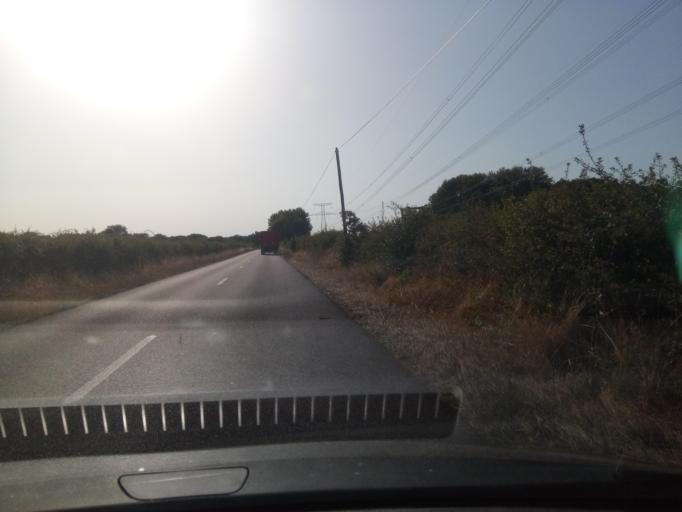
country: FR
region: Poitou-Charentes
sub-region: Departement de la Vienne
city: Montmorillon
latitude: 46.4455
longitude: 0.9739
